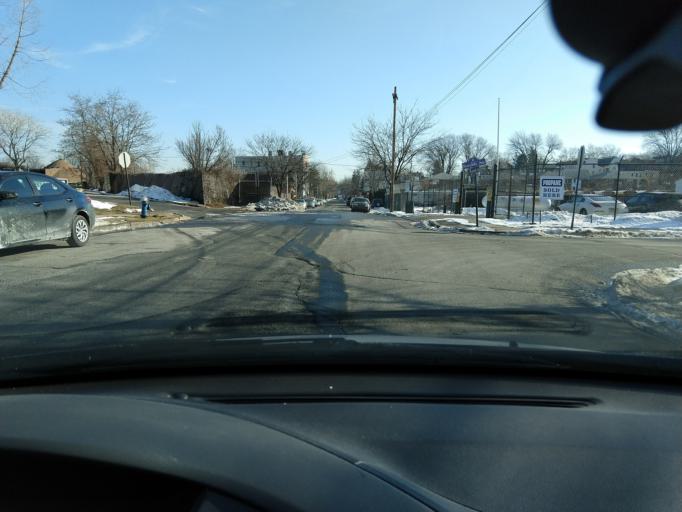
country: US
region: New Jersey
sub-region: Essex County
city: Orange
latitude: 40.7827
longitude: -74.2322
